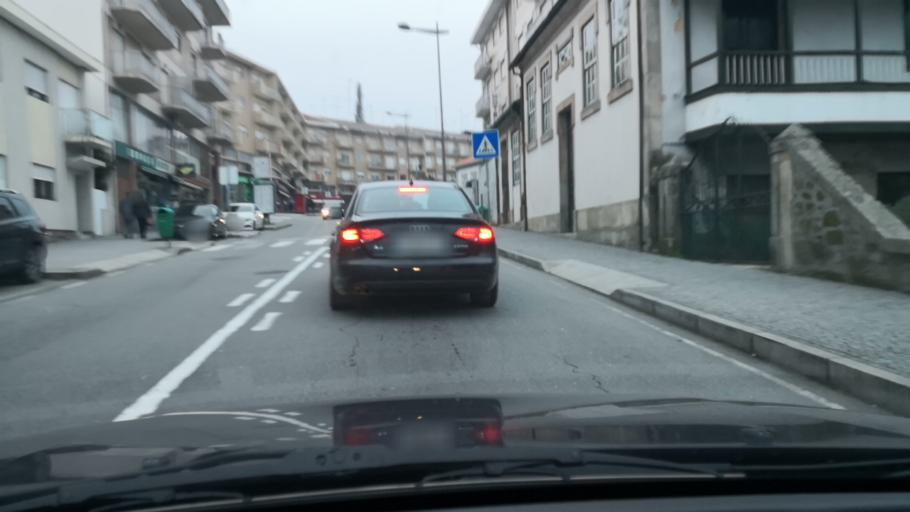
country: PT
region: Viseu
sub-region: Lamego
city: Lamego
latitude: 41.0980
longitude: -7.8110
